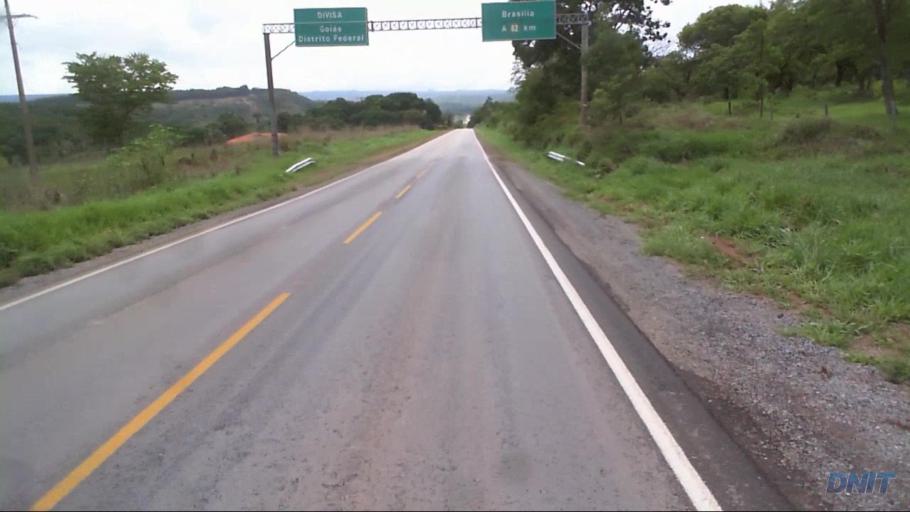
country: BR
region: Goias
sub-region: Padre Bernardo
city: Padre Bernardo
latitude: -15.5103
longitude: -48.1966
